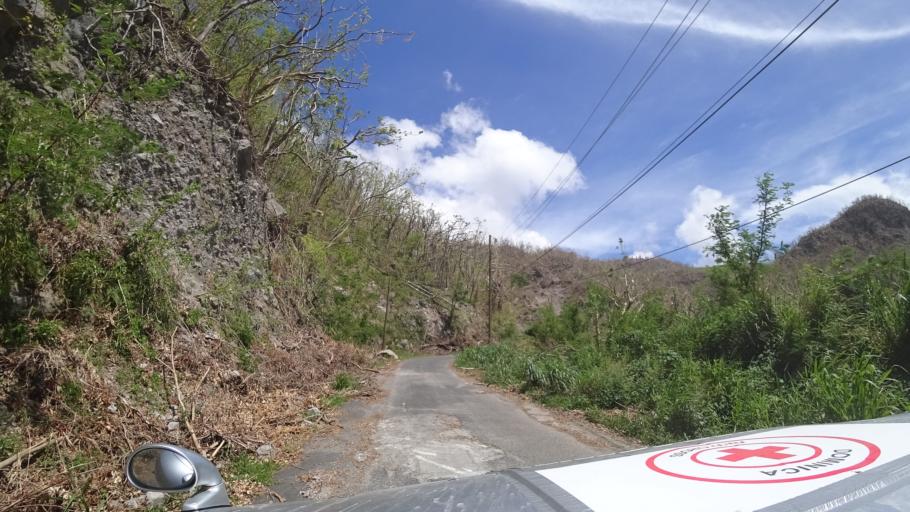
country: DM
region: Saint Mark
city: Soufriere
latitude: 15.2428
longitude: -61.3706
